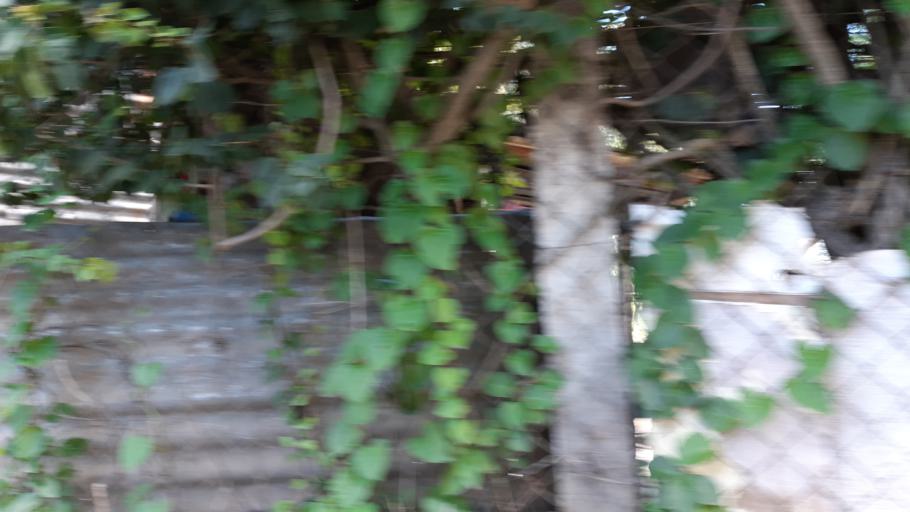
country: GT
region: Chimaltenango
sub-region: Municipio de Chimaltenango
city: Chimaltenango
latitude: 14.6676
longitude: -90.8501
